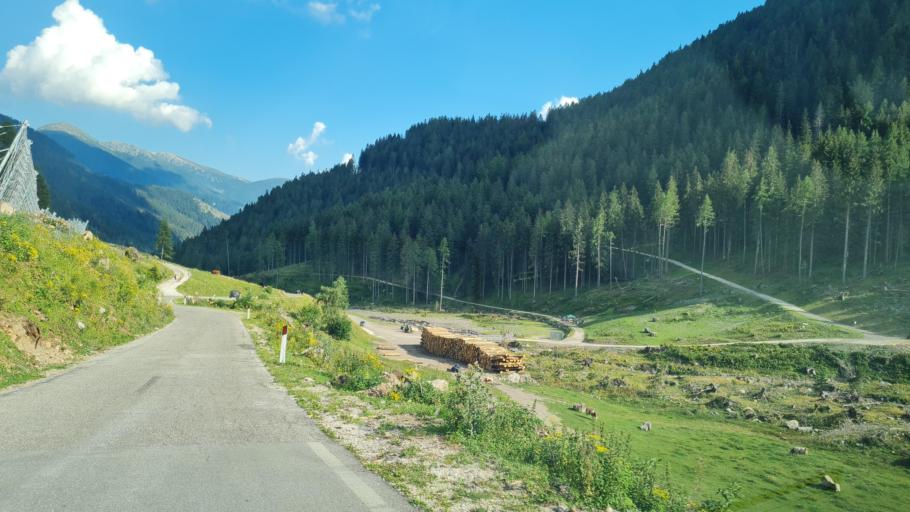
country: IT
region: Trentino-Alto Adige
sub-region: Provincia di Trento
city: Torcegno
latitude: 46.1519
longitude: 11.4446
